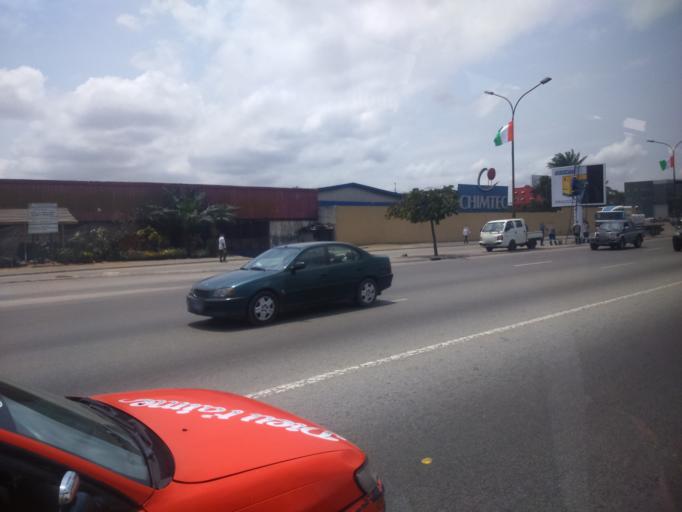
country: CI
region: Lagunes
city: Abidjan
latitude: 5.3012
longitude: -3.9908
